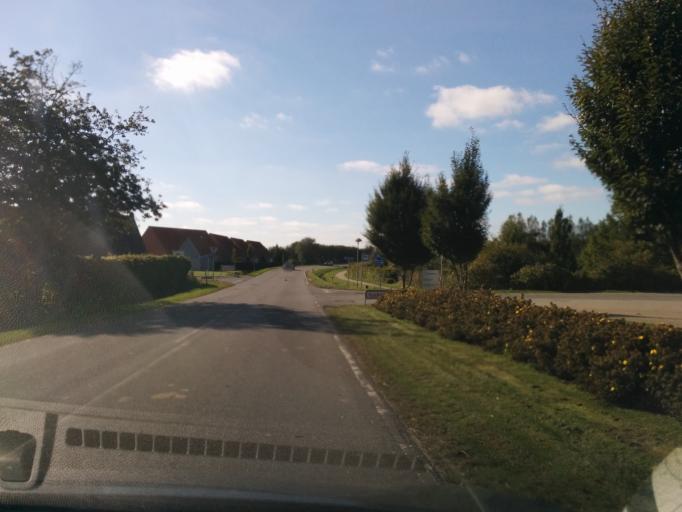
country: DK
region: South Denmark
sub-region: Kolding Kommune
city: Sonder Bjert
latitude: 55.4057
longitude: 9.5483
